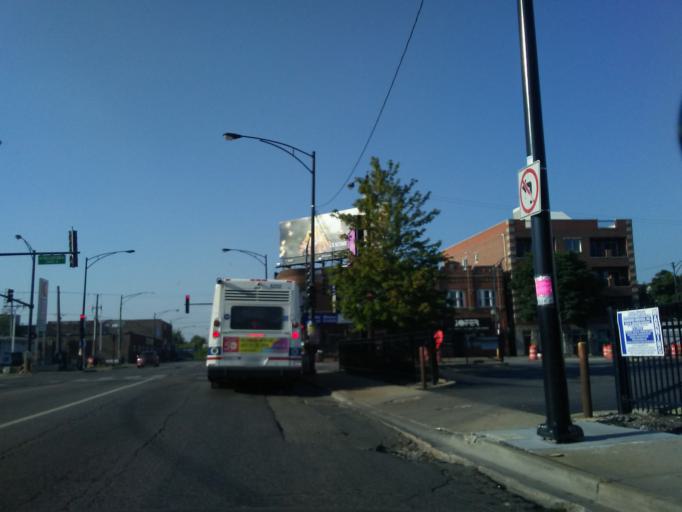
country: US
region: Illinois
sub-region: Cook County
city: Oak Park
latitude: 41.9249
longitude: -87.7269
